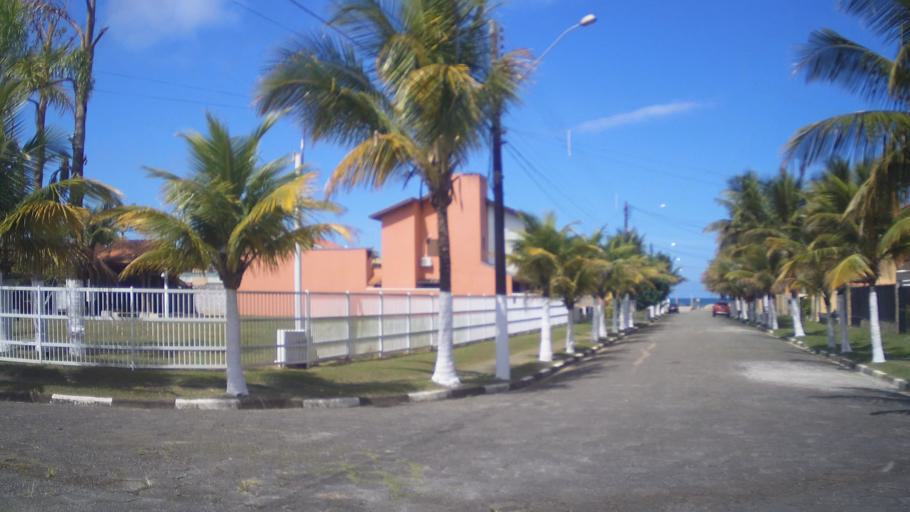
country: BR
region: Sao Paulo
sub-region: Itanhaem
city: Itanhaem
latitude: -24.1485
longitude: -46.7217
